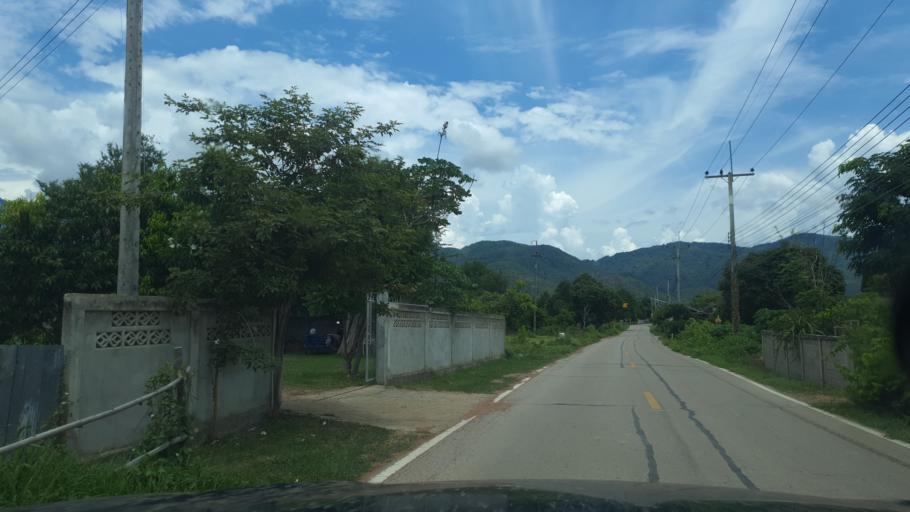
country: TH
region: Lampang
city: Sop Prap
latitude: 17.9114
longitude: 99.4130
